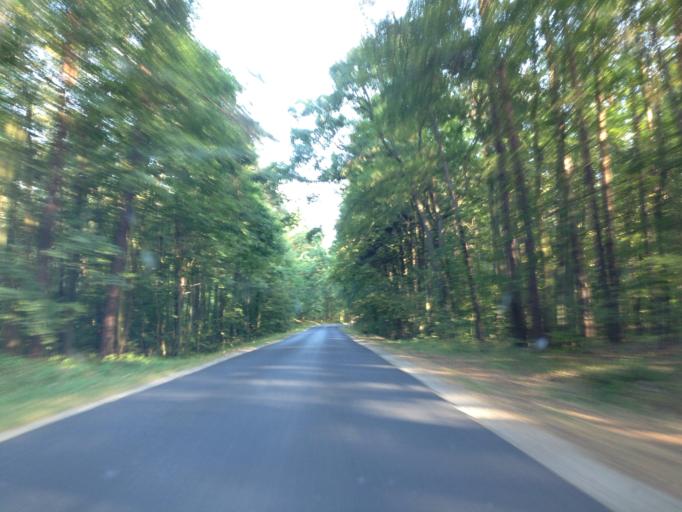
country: PL
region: Kujawsko-Pomorskie
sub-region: Powiat brodnicki
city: Brodnica
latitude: 53.3605
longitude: 19.3820
